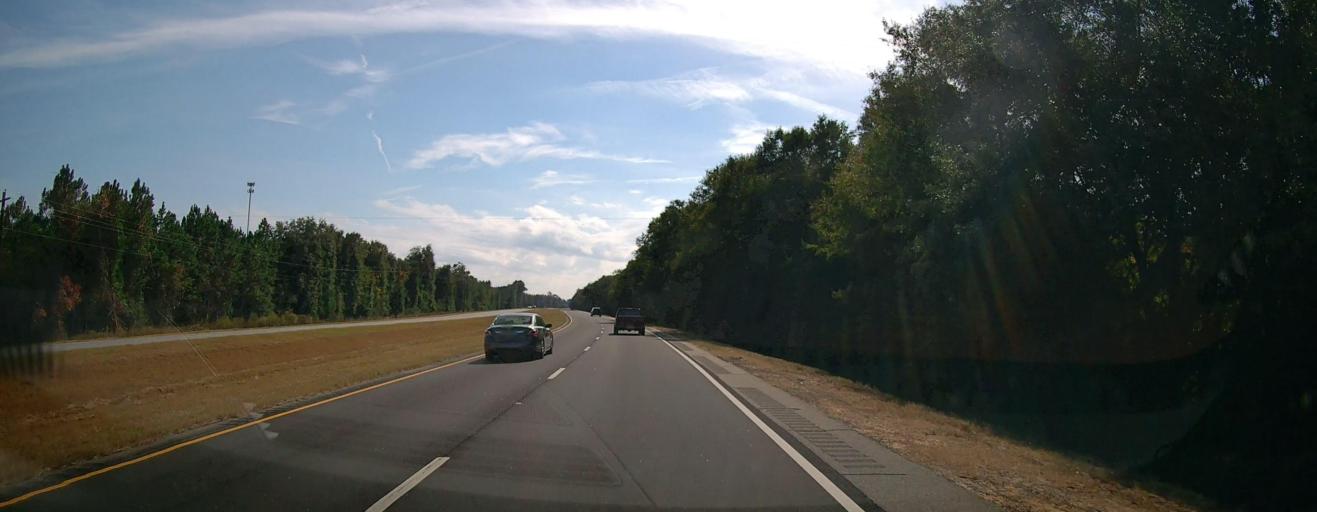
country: US
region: Georgia
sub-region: Dougherty County
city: Putney
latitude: 31.4003
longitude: -84.1456
